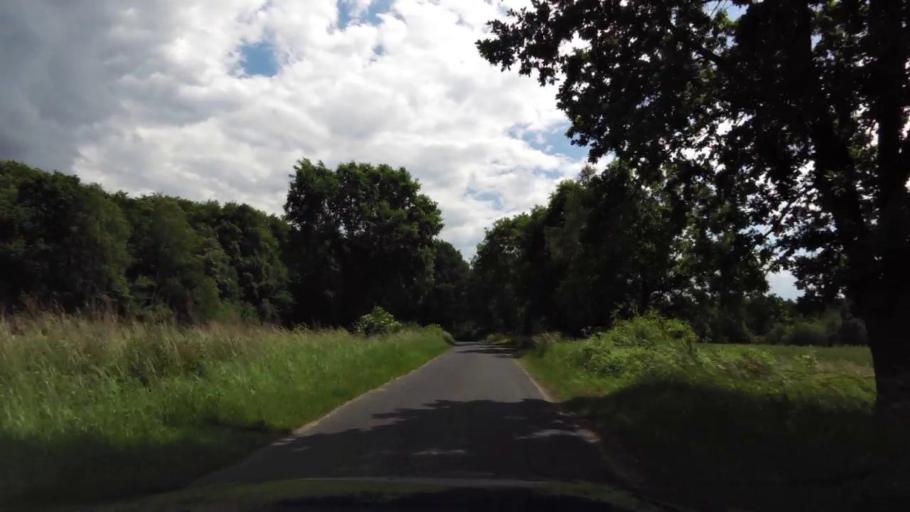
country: PL
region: West Pomeranian Voivodeship
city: Trzcinsko Zdroj
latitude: 52.8984
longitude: 14.6100
